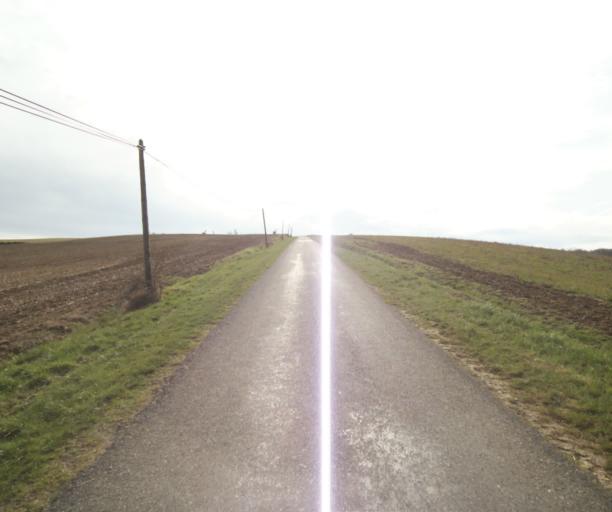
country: FR
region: Aquitaine
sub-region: Departement des Landes
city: Gabarret
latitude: 43.9408
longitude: 0.0458
